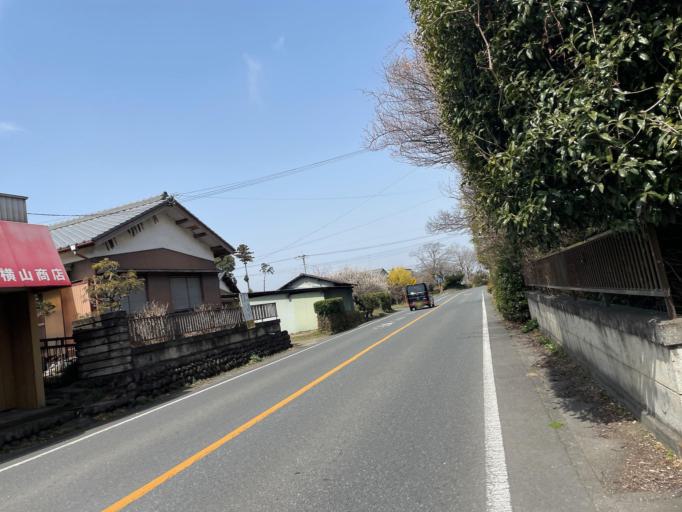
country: JP
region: Saitama
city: Ogawa
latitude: 36.0718
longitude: 139.2967
